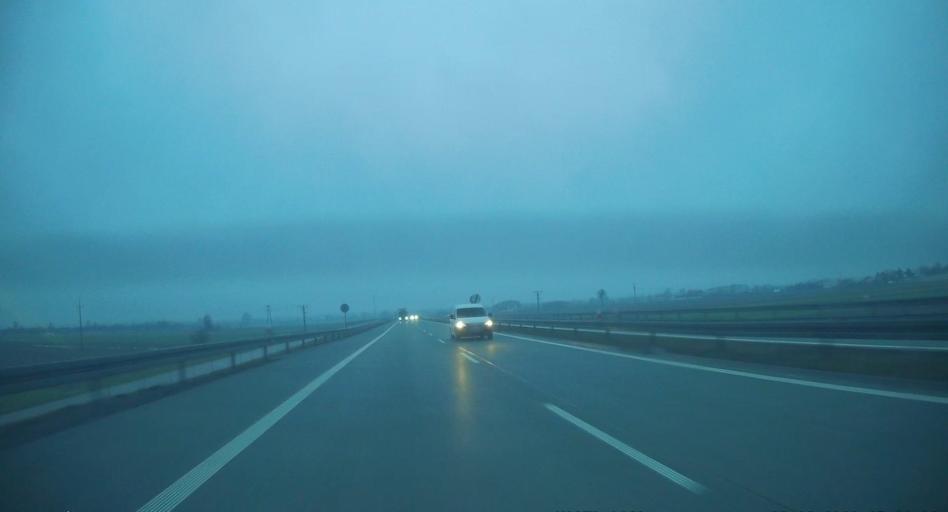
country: PL
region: Lodz Voivodeship
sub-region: Powiat tomaszowski
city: Lubochnia
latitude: 51.6181
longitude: 20.0912
